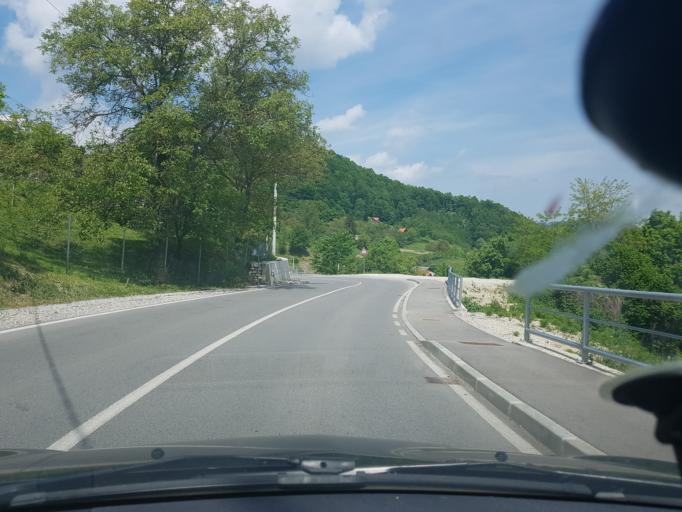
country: SI
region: Rogatec
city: Rogatec
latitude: 46.2139
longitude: 15.6899
